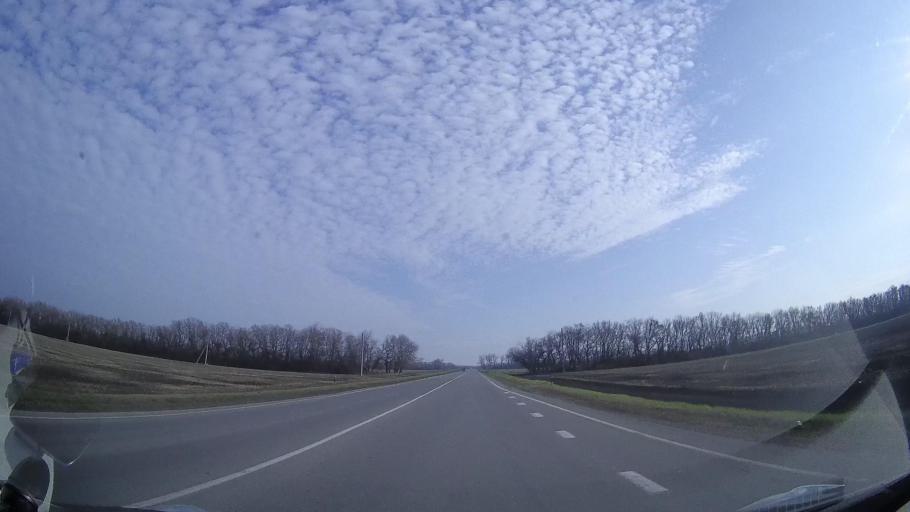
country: RU
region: Rostov
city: Tselina
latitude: 46.5230
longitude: 41.1271
